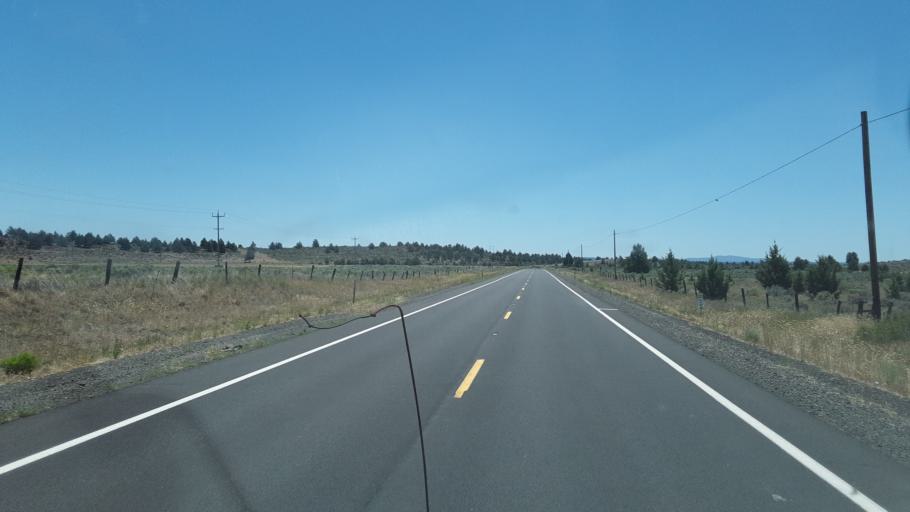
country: US
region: California
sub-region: Siskiyou County
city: Tulelake
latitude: 41.7169
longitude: -121.2898
